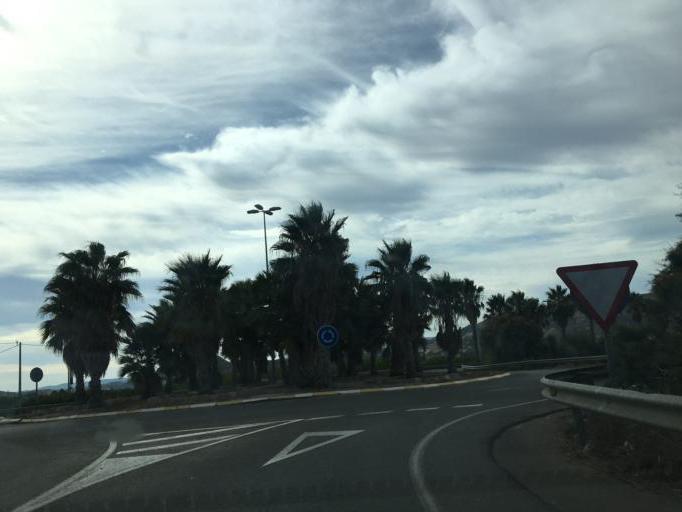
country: ES
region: Murcia
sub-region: Murcia
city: Santomera
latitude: 38.0111
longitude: -1.0397
